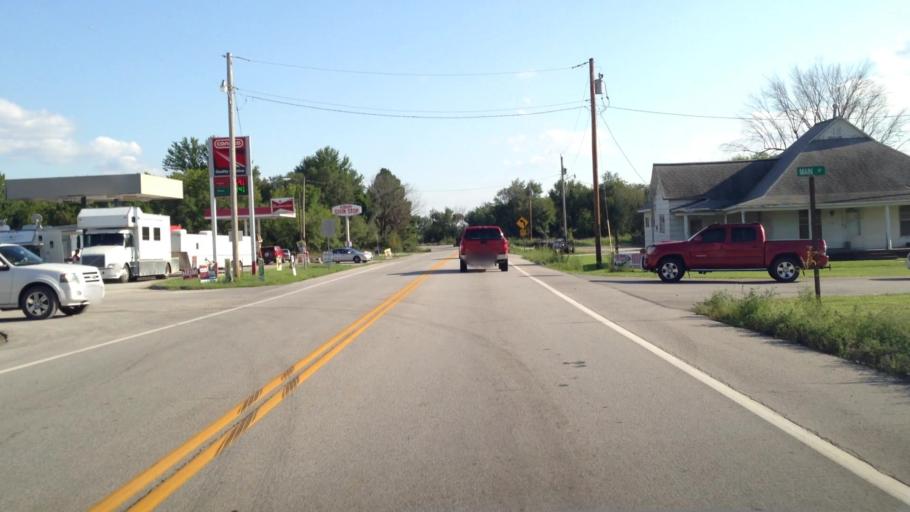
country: US
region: Missouri
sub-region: Jasper County
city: Carl Junction
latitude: 37.2746
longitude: -94.6011
